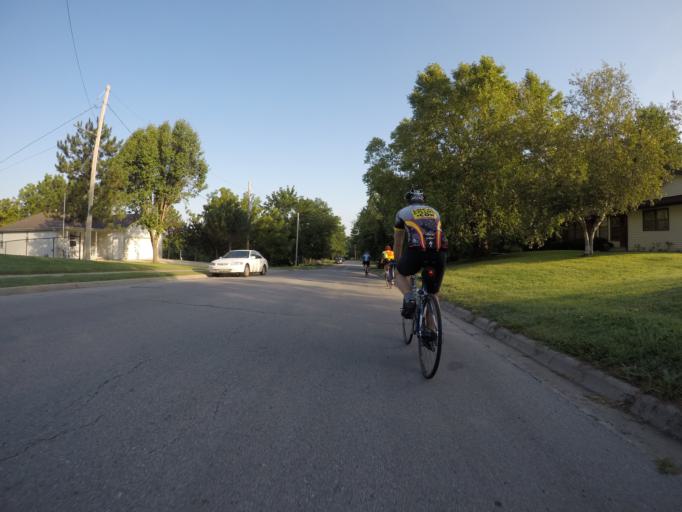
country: US
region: Kansas
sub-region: Leavenworth County
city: Leavenworth
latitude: 39.2936
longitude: -94.9000
